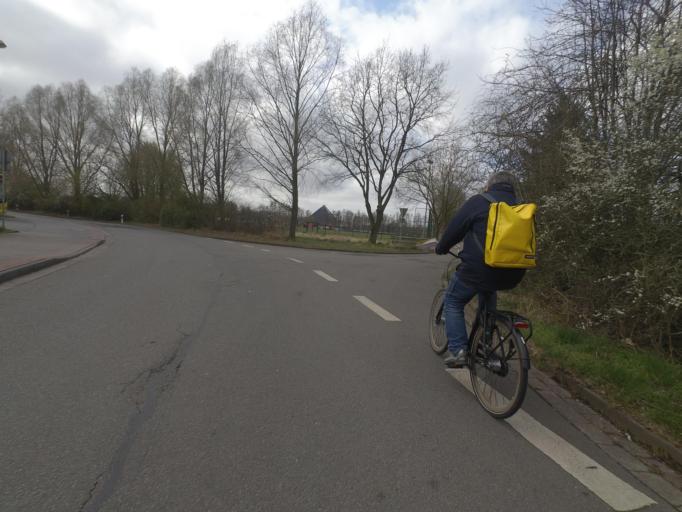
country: DE
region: Lower Saxony
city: Oldenburg
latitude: 53.1641
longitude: 8.1766
